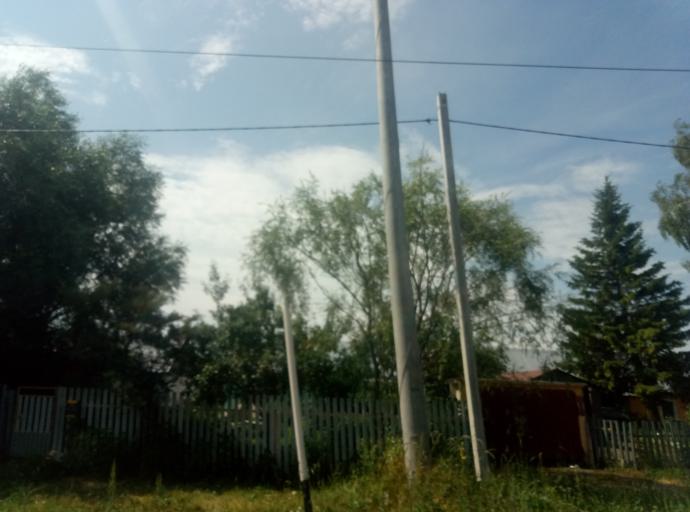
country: RU
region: Tula
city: Dubovka
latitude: 53.8997
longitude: 38.0371
